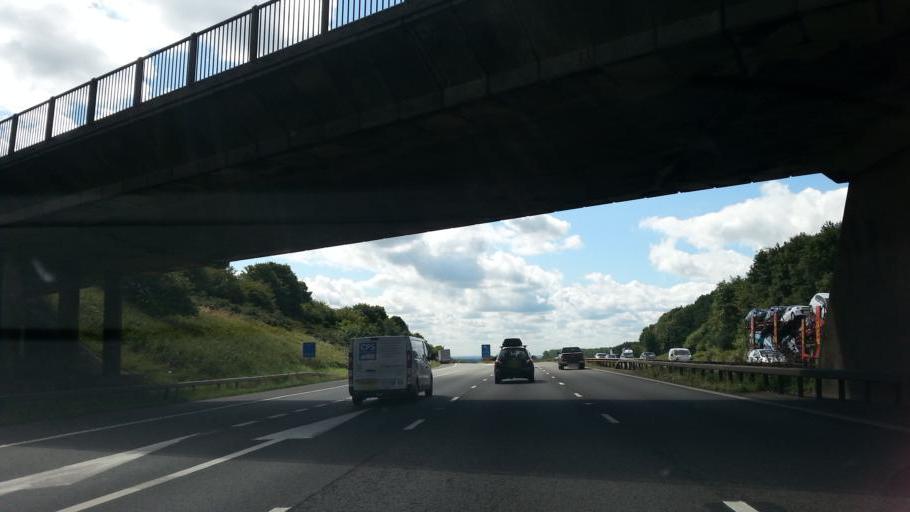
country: GB
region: England
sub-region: Leicestershire
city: Markfield
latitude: 52.7043
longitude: -1.2920
